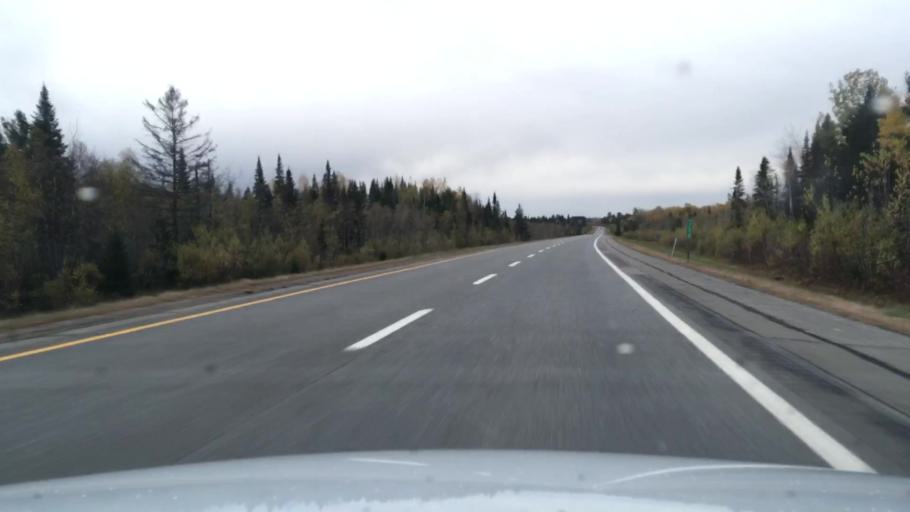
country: US
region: Maine
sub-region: Penobscot County
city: Greenbush
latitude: 45.1169
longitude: -68.6949
